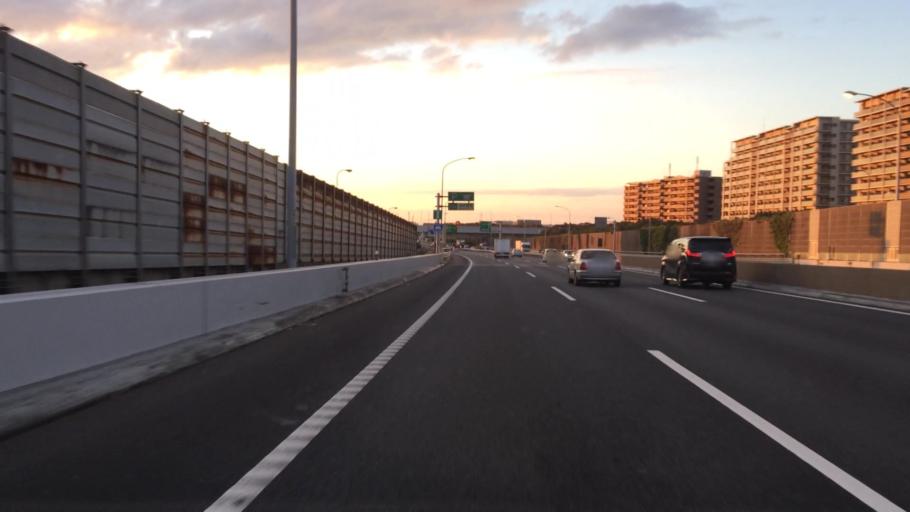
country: JP
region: Chiba
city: Funabashi
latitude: 35.6570
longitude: 140.0380
